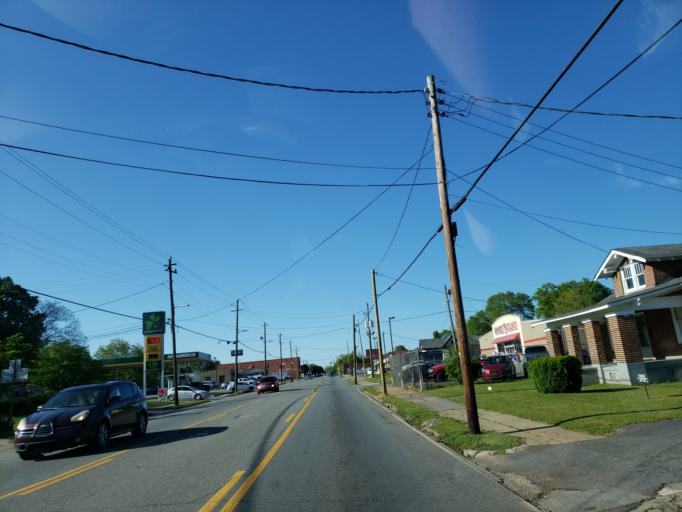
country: US
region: Georgia
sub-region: Polk County
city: Cedartown
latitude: 34.0064
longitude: -85.2550
